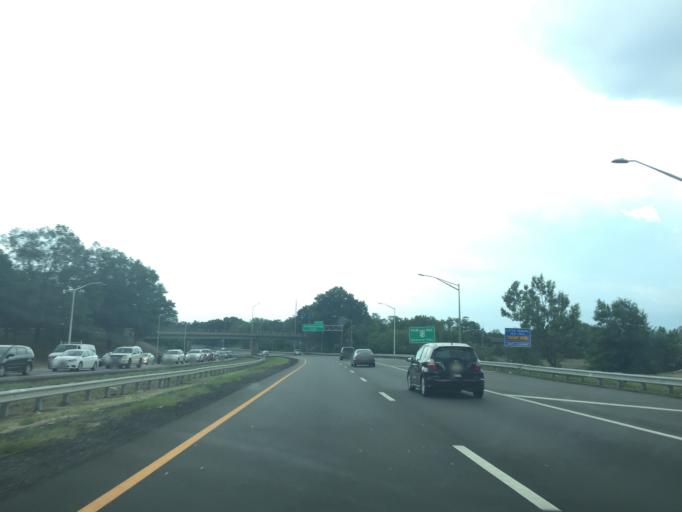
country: US
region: New York
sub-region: Richmond County
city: Bloomfield
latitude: 40.6238
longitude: -74.1767
